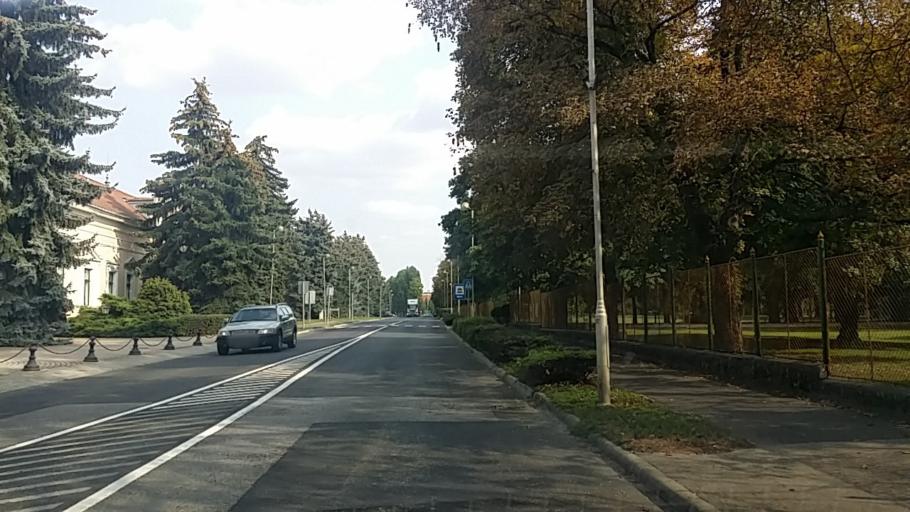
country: HU
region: Komarom-Esztergom
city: Babolna
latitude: 47.6414
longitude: 17.9807
